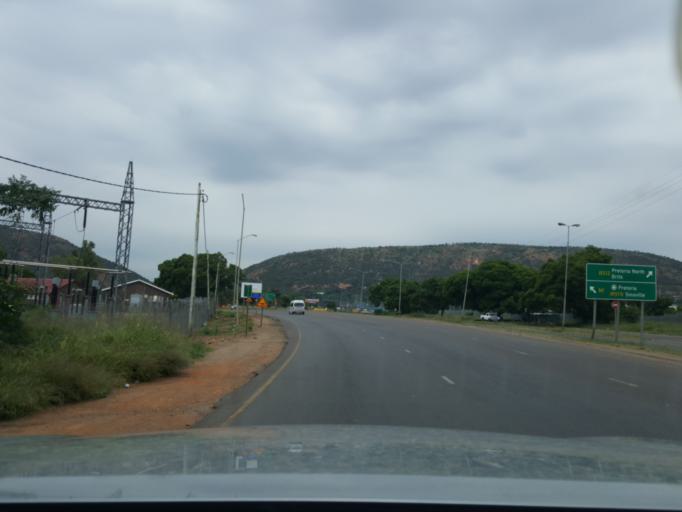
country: ZA
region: Gauteng
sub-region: City of Tshwane Metropolitan Municipality
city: Pretoria
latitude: -25.6755
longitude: 28.1828
